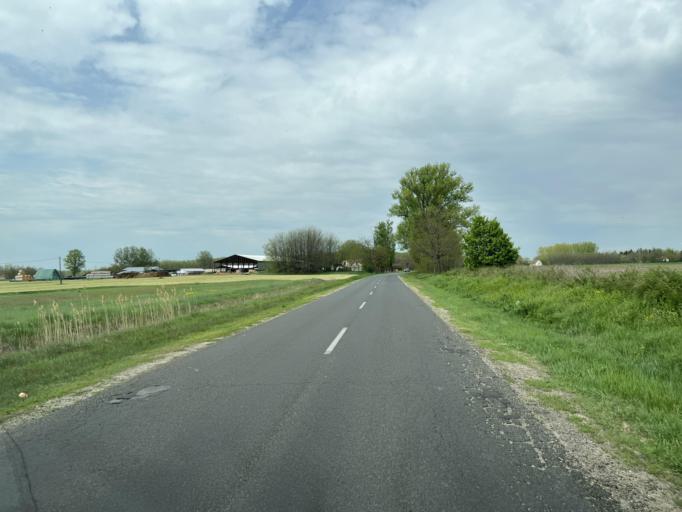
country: HU
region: Pest
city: Tortel
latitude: 47.1400
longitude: 19.8864
